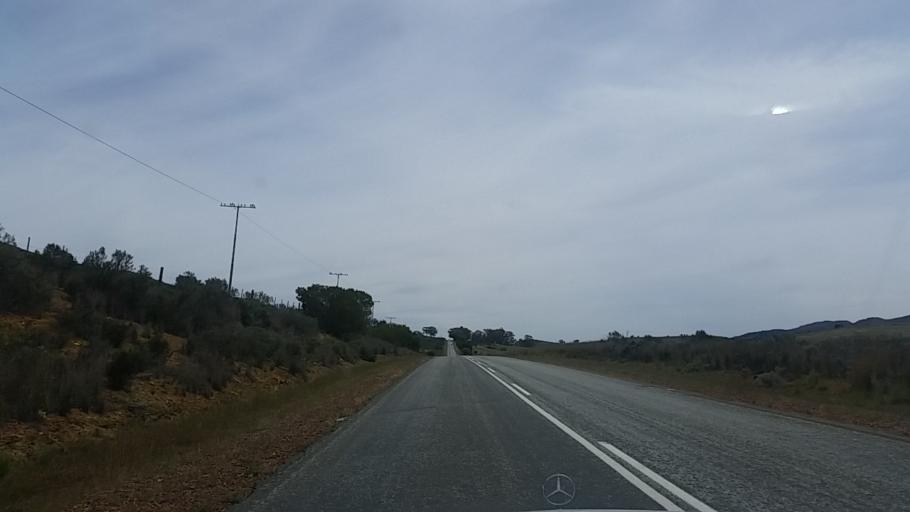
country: ZA
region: Western Cape
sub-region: Eden District Municipality
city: Knysna
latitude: -33.7726
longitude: 22.9346
